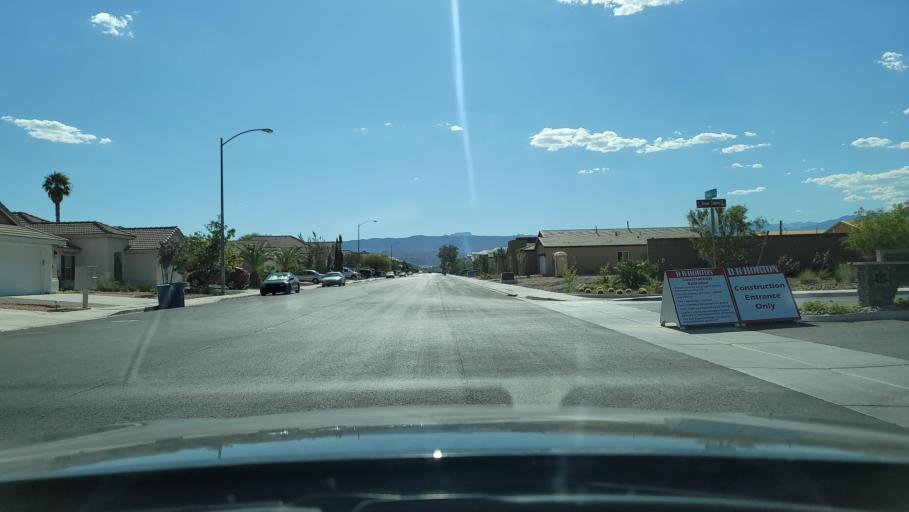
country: US
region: Nevada
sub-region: Clark County
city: Spring Valley
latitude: 36.0887
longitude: -115.2551
